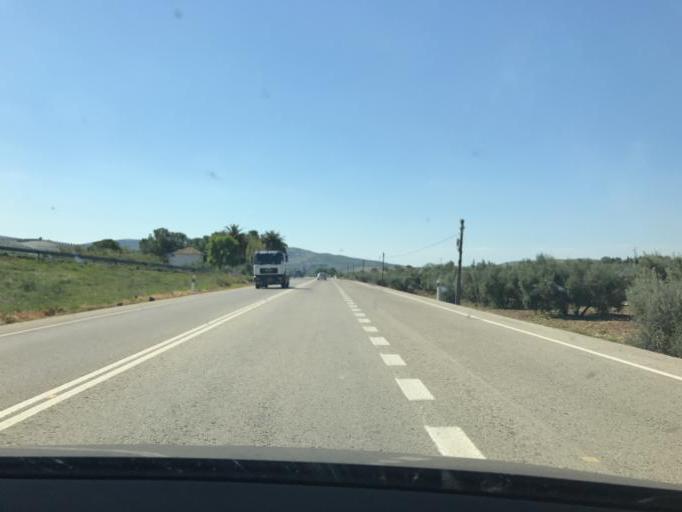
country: ES
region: Andalusia
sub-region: Province of Cordoba
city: Luque
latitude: 37.5766
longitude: -4.2724
